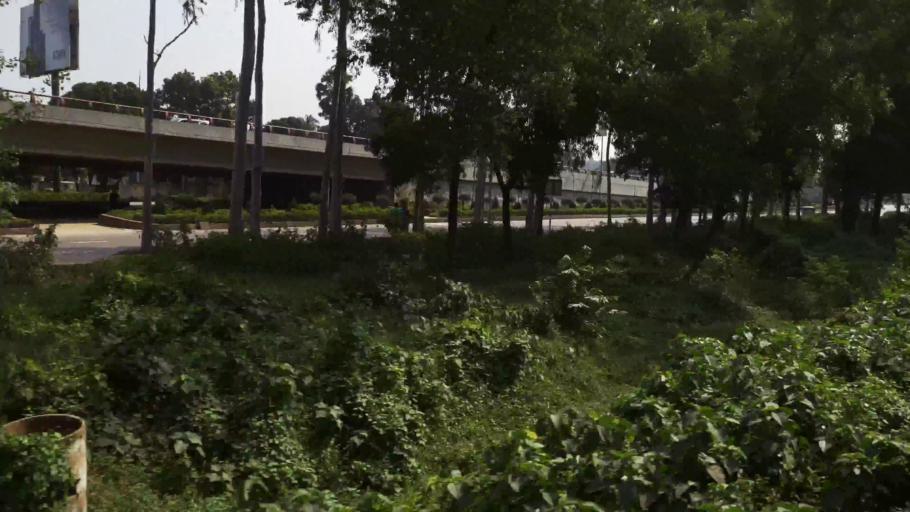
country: BD
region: Dhaka
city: Tungi
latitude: 23.8417
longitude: 90.4168
